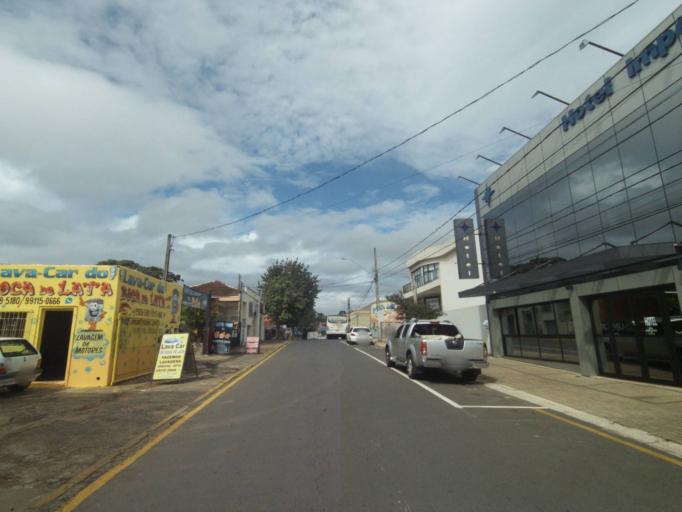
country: BR
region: Parana
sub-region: Telemaco Borba
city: Telemaco Borba
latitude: -24.3280
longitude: -50.6244
